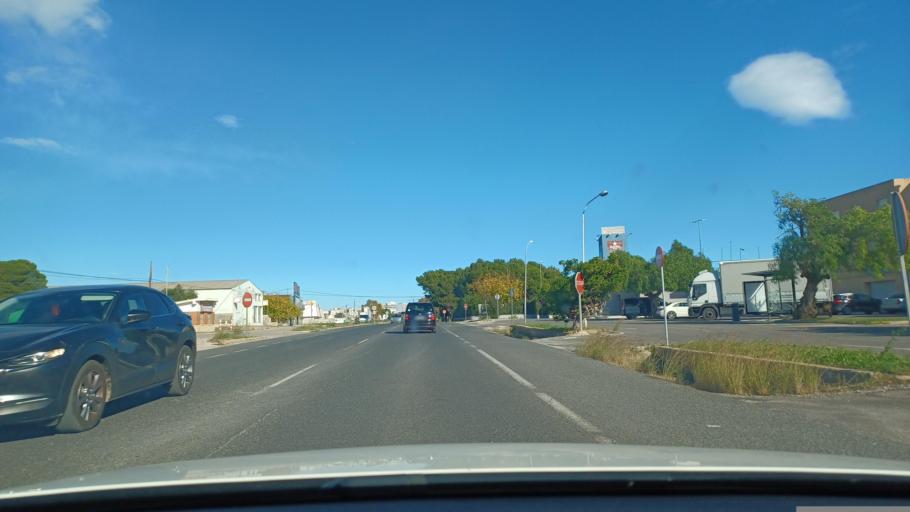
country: ES
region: Valencia
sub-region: Provincia de Castello
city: Vinaros
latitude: 40.4582
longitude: 0.4588
